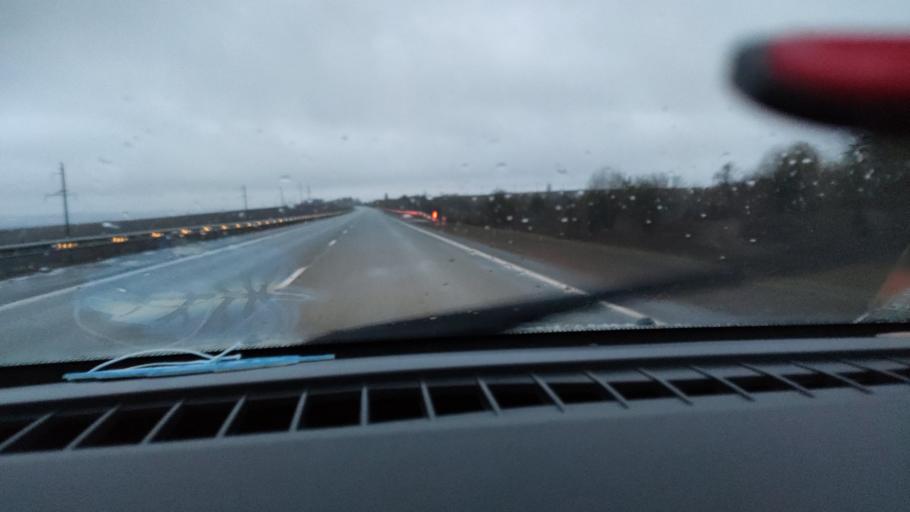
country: RU
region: Udmurtiya
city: Alnashi
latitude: 56.2267
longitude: 52.4110
